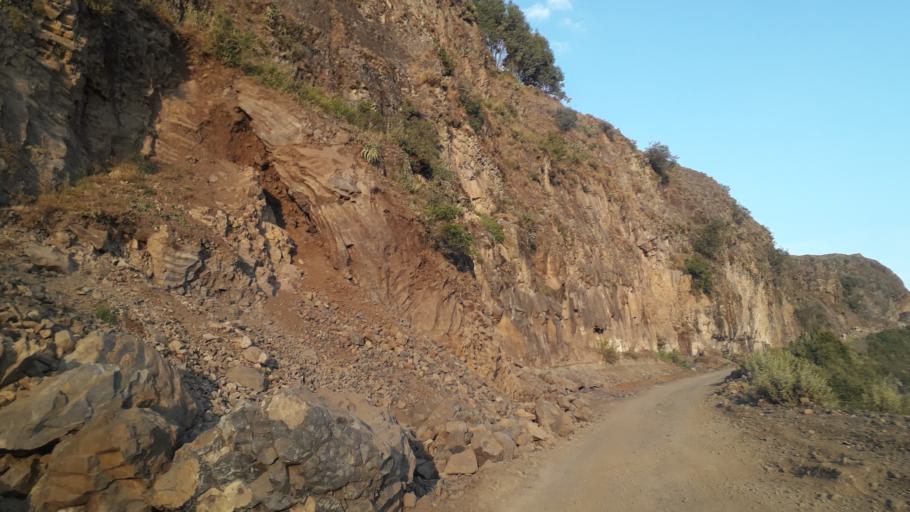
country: ET
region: Amhara
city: Lalibela
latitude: 11.5538
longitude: 39.2187
